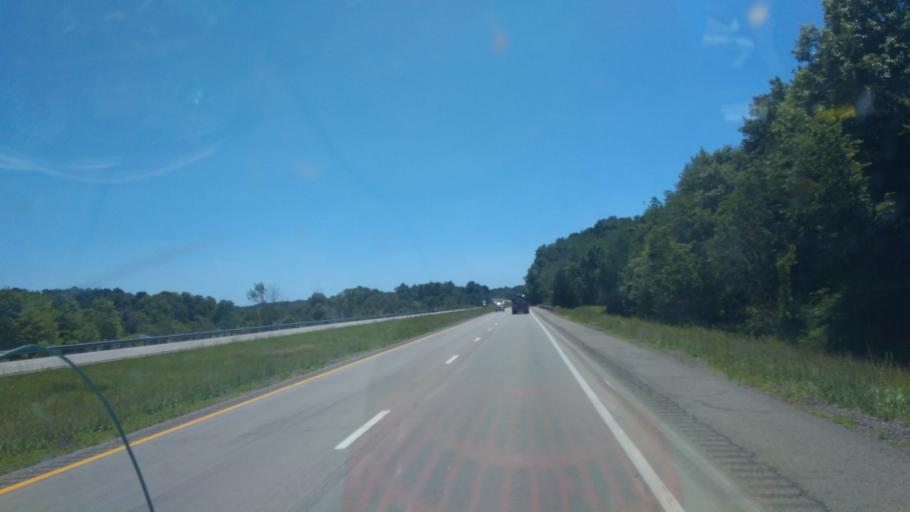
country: US
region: Ohio
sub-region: Columbiana County
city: Lisbon
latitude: 40.8125
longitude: -80.7461
